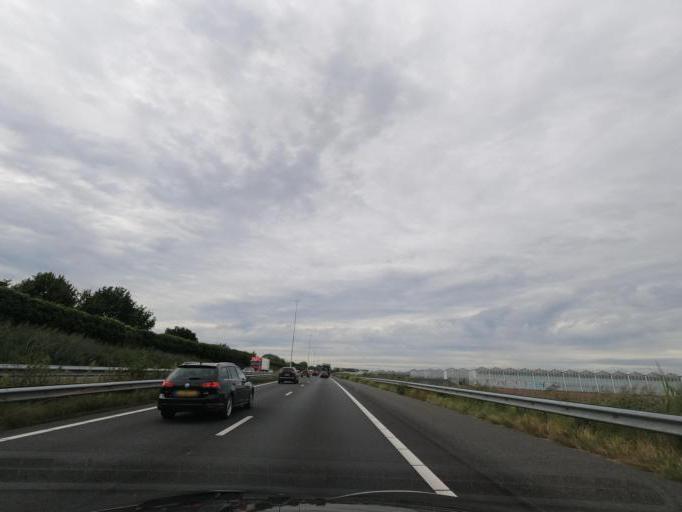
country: NL
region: North Brabant
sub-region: Gemeente Heusden
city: Heusden
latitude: 51.6944
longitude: 5.1336
